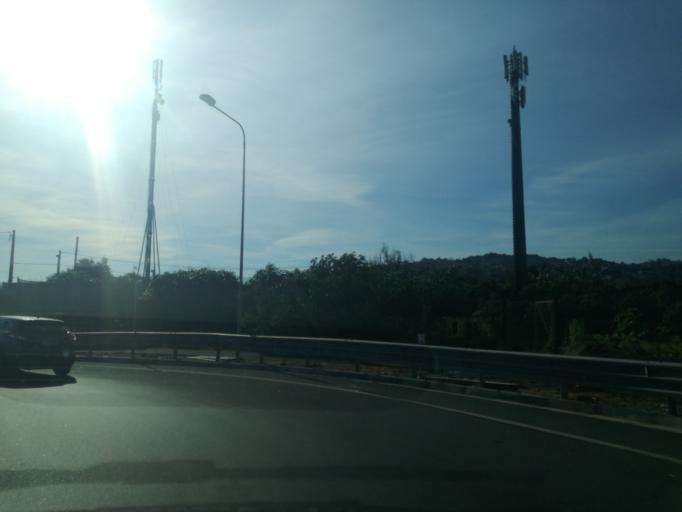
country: IT
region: Sicily
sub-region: Catania
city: Vambolieri
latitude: 37.5799
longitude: 15.1678
